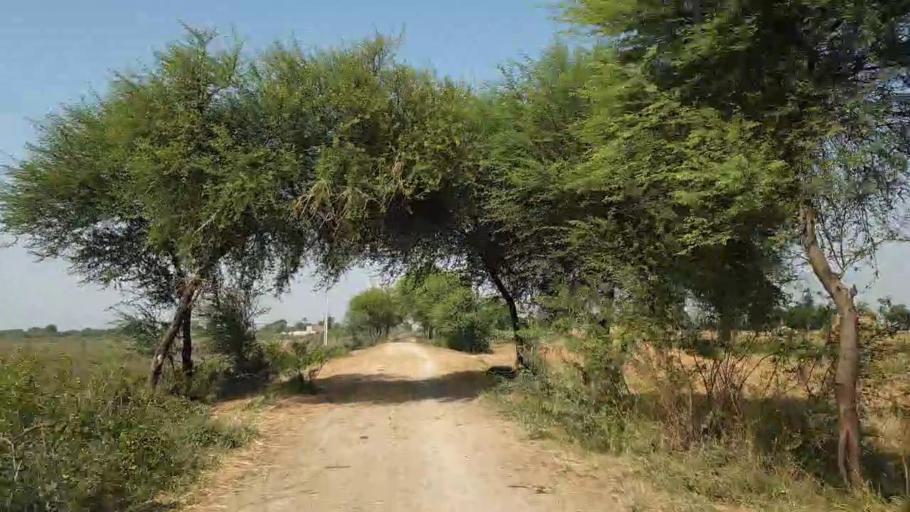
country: PK
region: Sindh
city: Tando Muhammad Khan
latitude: 25.0317
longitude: 68.4049
